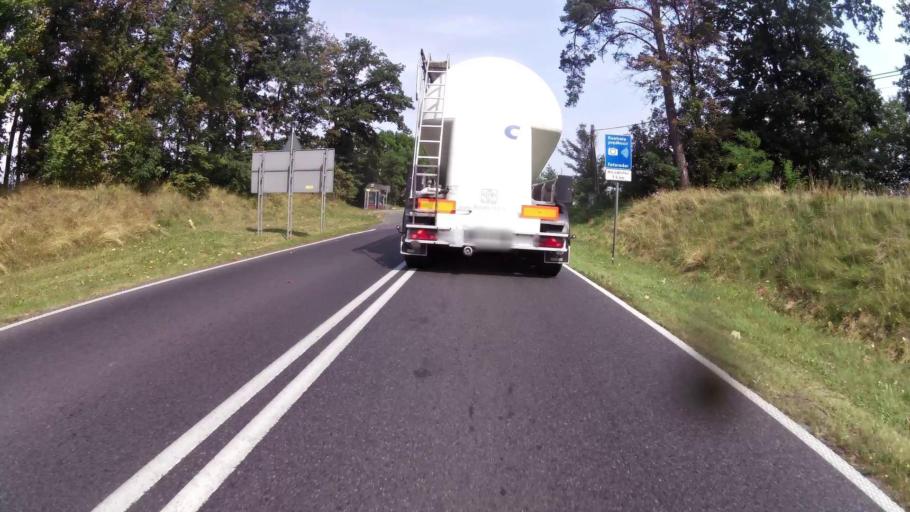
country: PL
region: West Pomeranian Voivodeship
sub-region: Powiat pyrzycki
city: Lipiany
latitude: 52.9453
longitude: 14.9515
